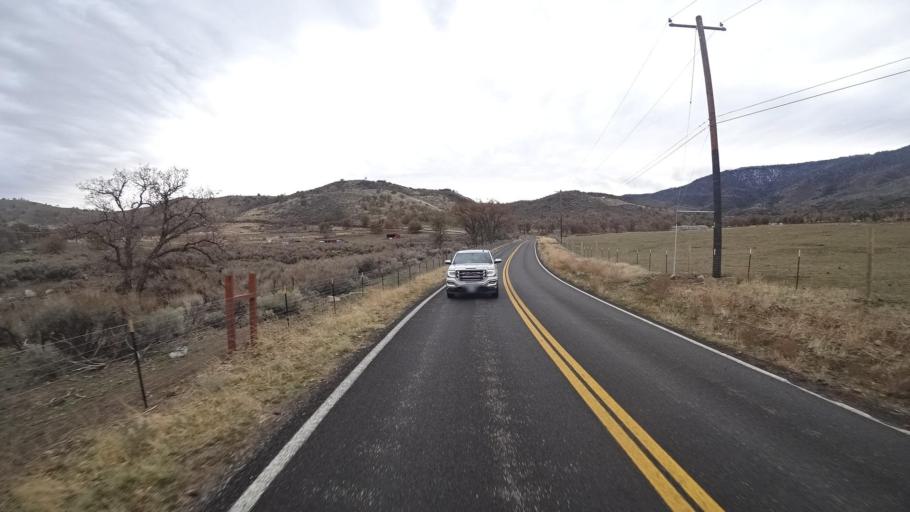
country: US
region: California
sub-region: Kern County
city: Stallion Springs
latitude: 35.0941
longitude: -118.5693
